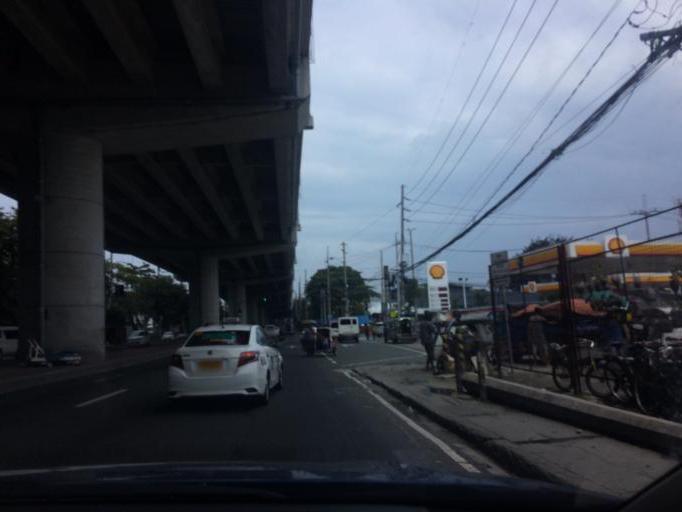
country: PH
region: Metro Manila
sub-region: Makati City
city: Makati City
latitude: 14.5278
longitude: 121.0056
